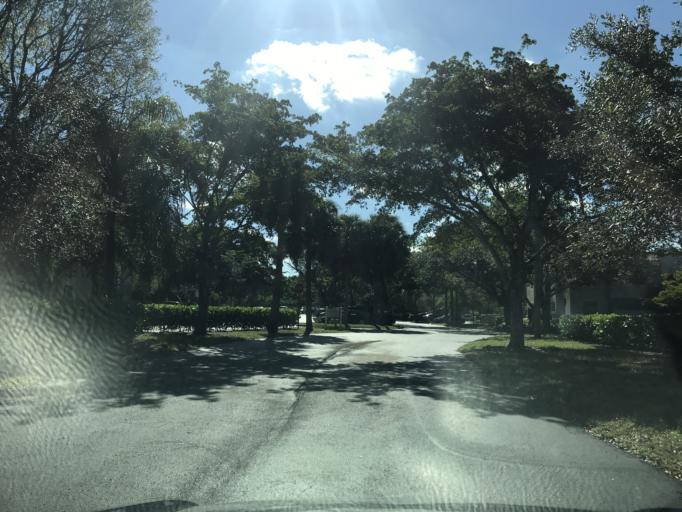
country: US
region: Florida
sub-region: Broward County
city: Pine Island Ridge
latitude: 26.1314
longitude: -80.2700
